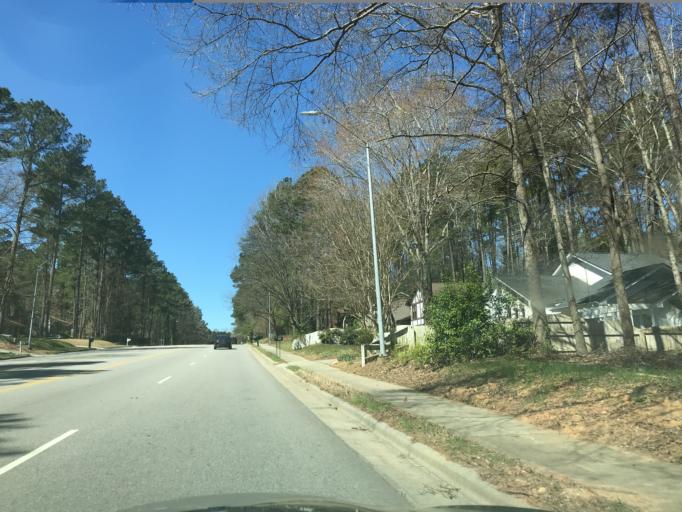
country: US
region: North Carolina
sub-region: Wake County
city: Garner
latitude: 35.6860
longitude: -78.6254
